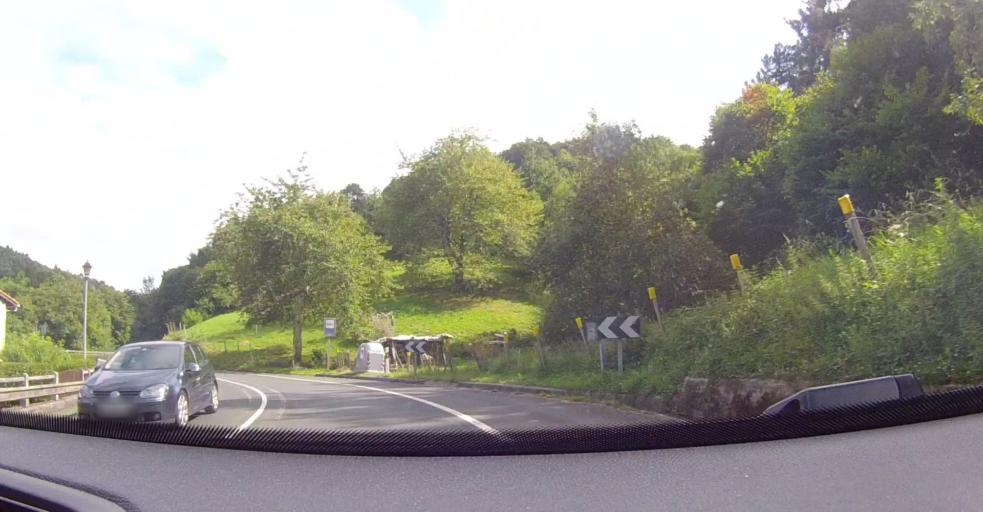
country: ES
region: Basque Country
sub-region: Bizkaia
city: Elantxobe
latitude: 43.3995
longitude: -2.6468
